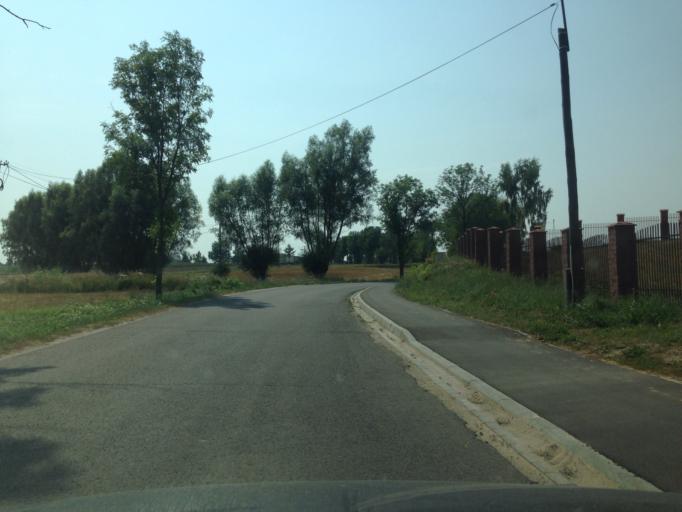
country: PL
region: Kujawsko-Pomorskie
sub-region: Powiat golubsko-dobrzynski
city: Golub-Dobrzyn
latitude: 53.0656
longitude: 19.0353
